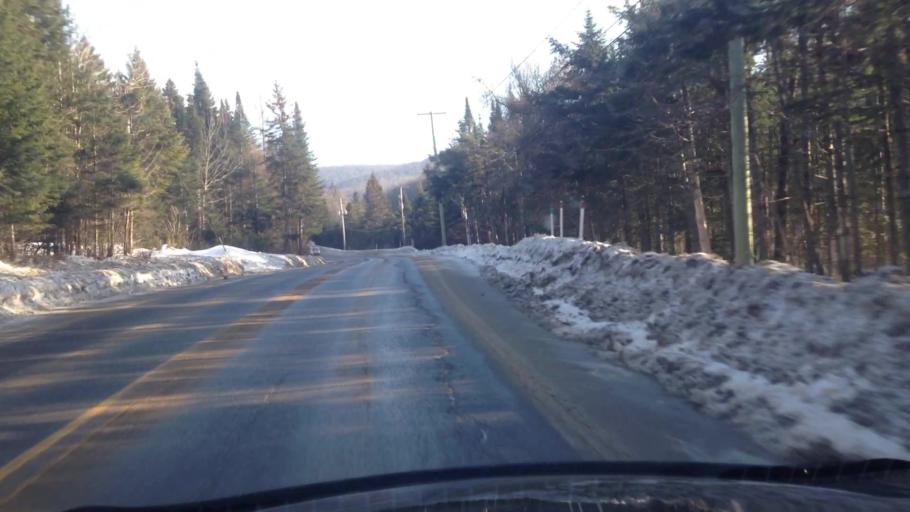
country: CA
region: Quebec
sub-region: Laurentides
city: Saint-Sauveur
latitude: 45.9071
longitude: -74.3260
